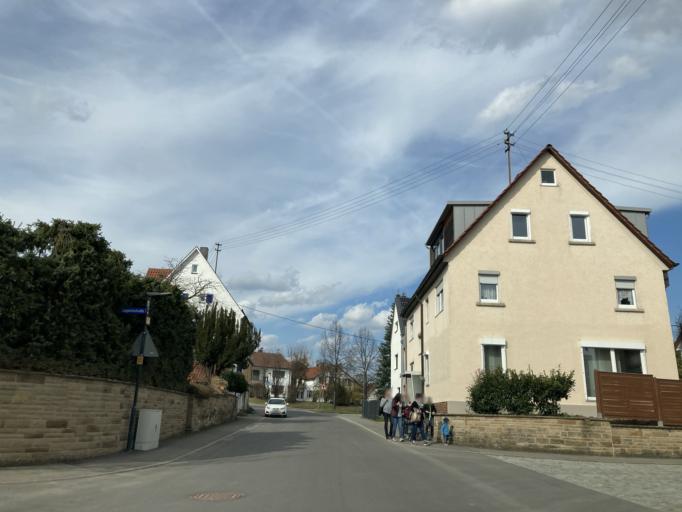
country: DE
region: Baden-Wuerttemberg
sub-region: Tuebingen Region
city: Kusterdingen
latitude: 48.5217
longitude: 9.1169
